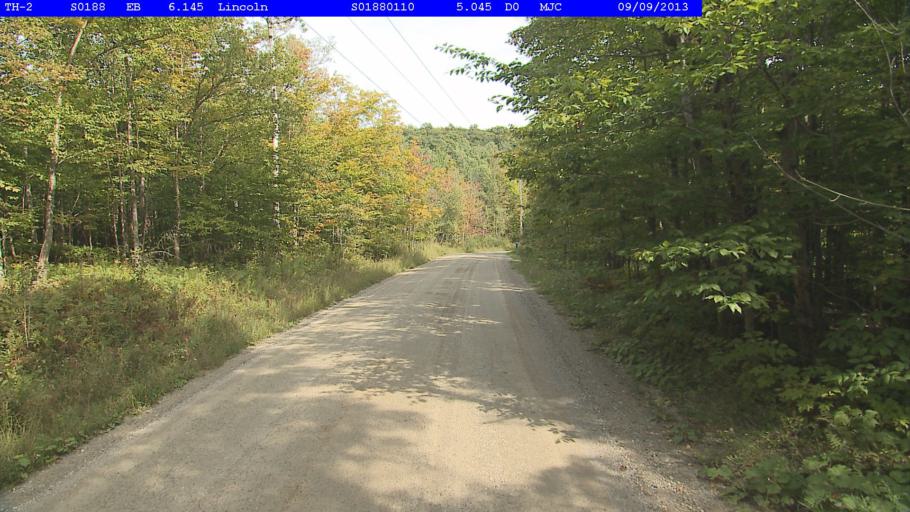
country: US
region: Vermont
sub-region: Addison County
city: Bristol
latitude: 44.0911
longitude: -72.9533
